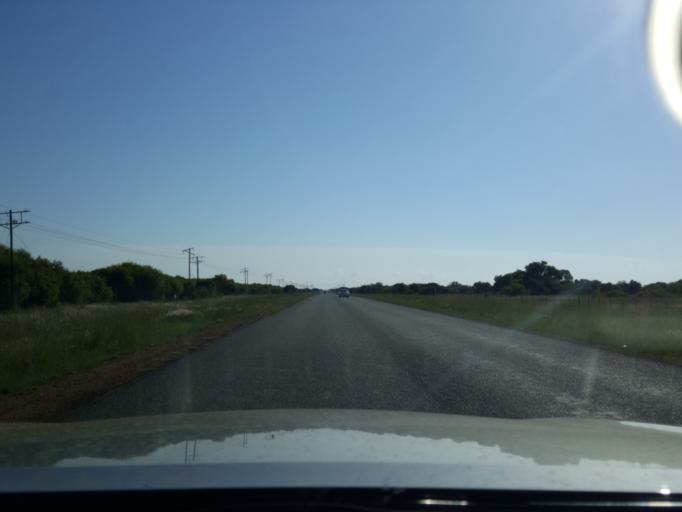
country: ZA
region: North-West
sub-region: Ngaka Modiri Molema District Municipality
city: Mahikeng
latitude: -25.8079
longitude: 25.8332
